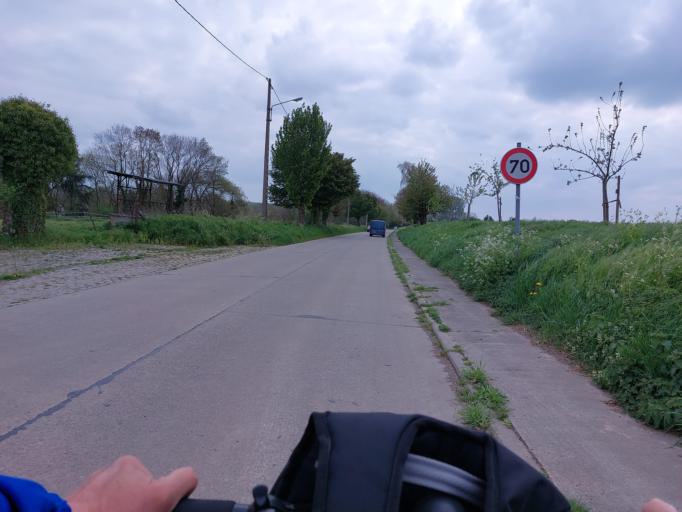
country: BE
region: Wallonia
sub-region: Province du Hainaut
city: Dour
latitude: 50.3683
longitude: 3.7283
